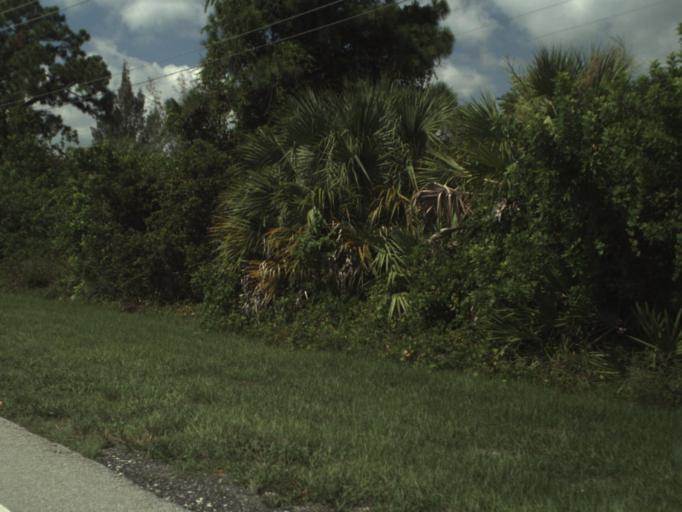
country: US
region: Florida
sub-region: Palm Beach County
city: Jupiter
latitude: 26.9156
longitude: -80.0942
